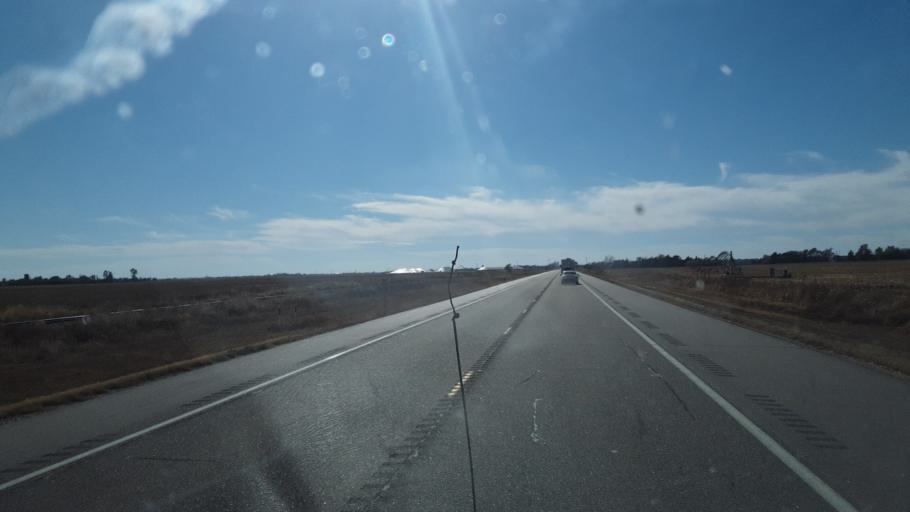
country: US
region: Kansas
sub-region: Pawnee County
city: Larned
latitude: 38.2143
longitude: -99.0523
